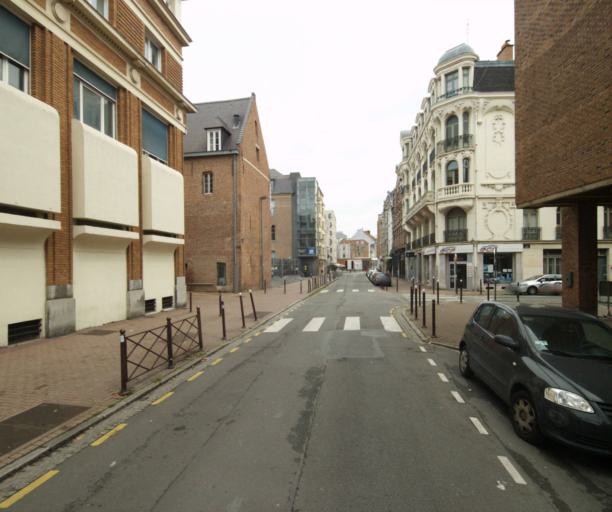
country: FR
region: Nord-Pas-de-Calais
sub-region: Departement du Nord
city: Lille
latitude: 50.6335
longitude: 3.0600
